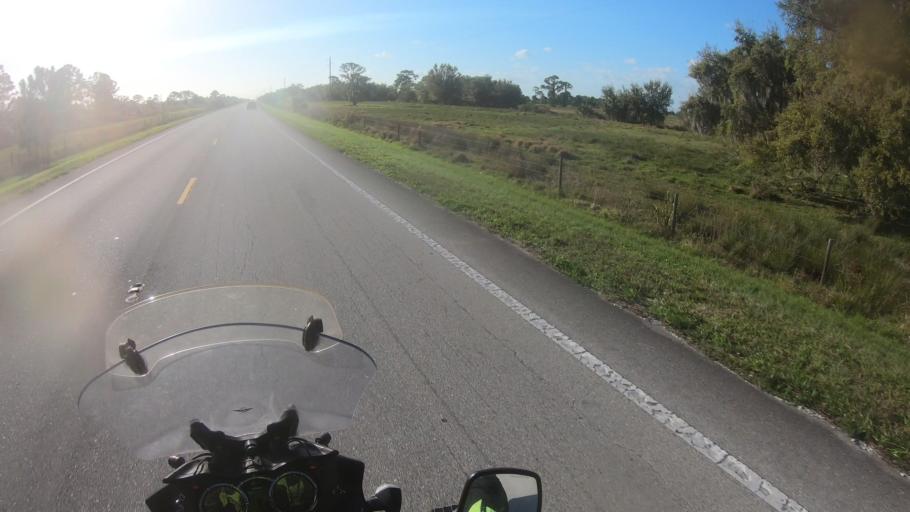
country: US
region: Florida
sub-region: Highlands County
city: Placid Lakes
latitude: 27.2091
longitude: -81.4718
